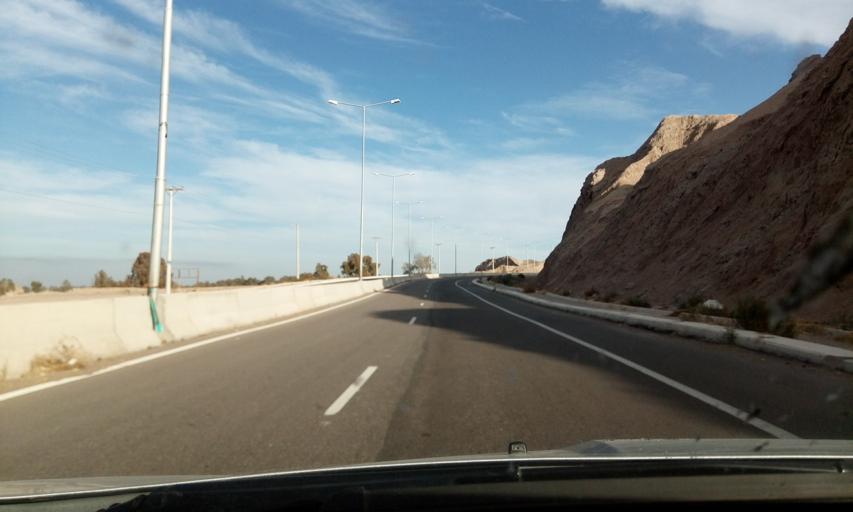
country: AR
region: San Juan
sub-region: Departamento de Rivadavia
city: Rivadavia
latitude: -31.4947
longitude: -68.6488
